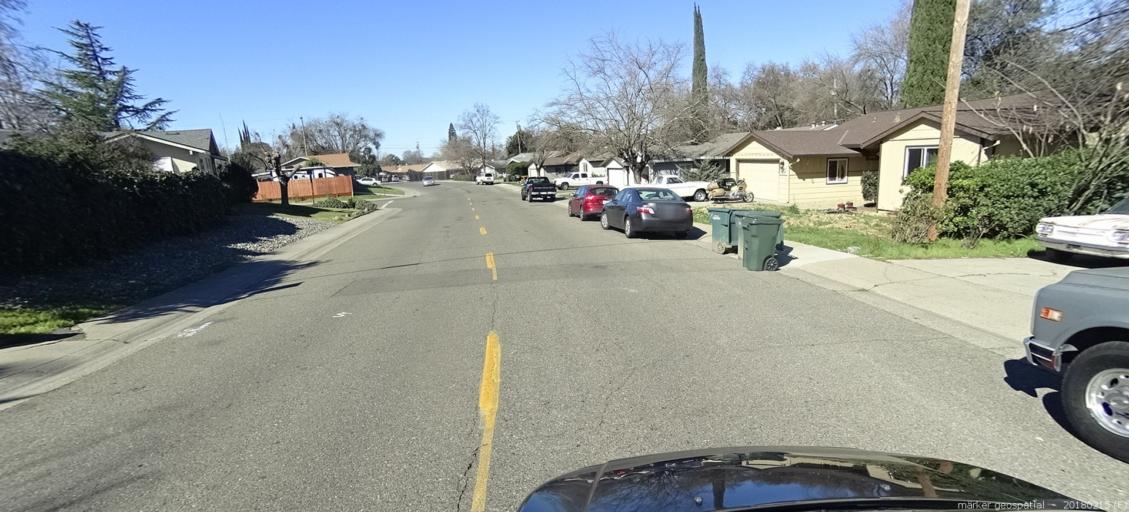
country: US
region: California
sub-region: Sacramento County
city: Foothill Farms
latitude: 38.6720
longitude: -121.3186
